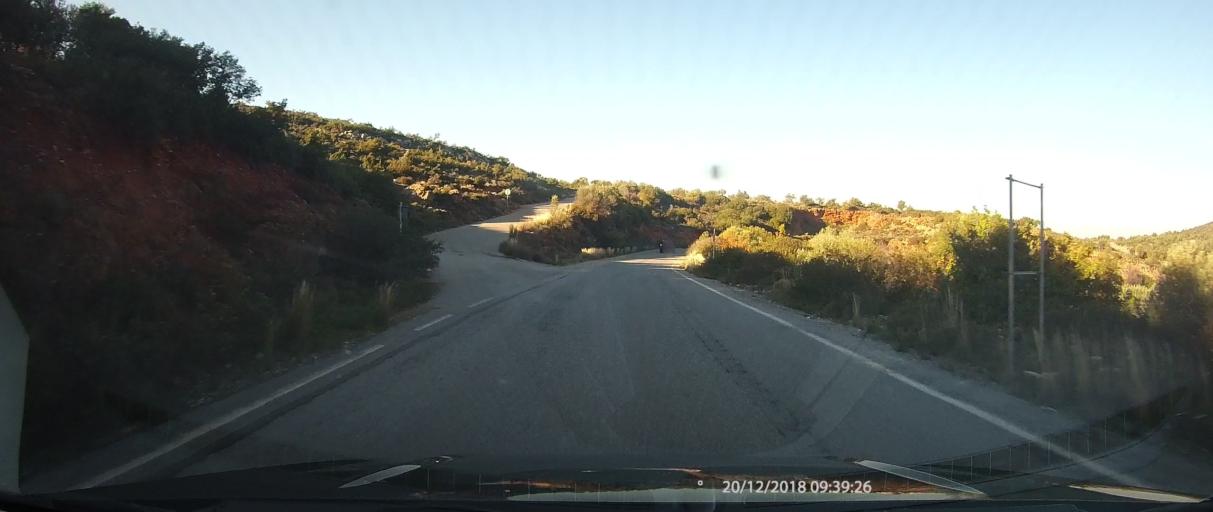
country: GR
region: Peloponnese
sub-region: Nomos Lakonias
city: Yerakion
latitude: 36.9397
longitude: 22.7758
